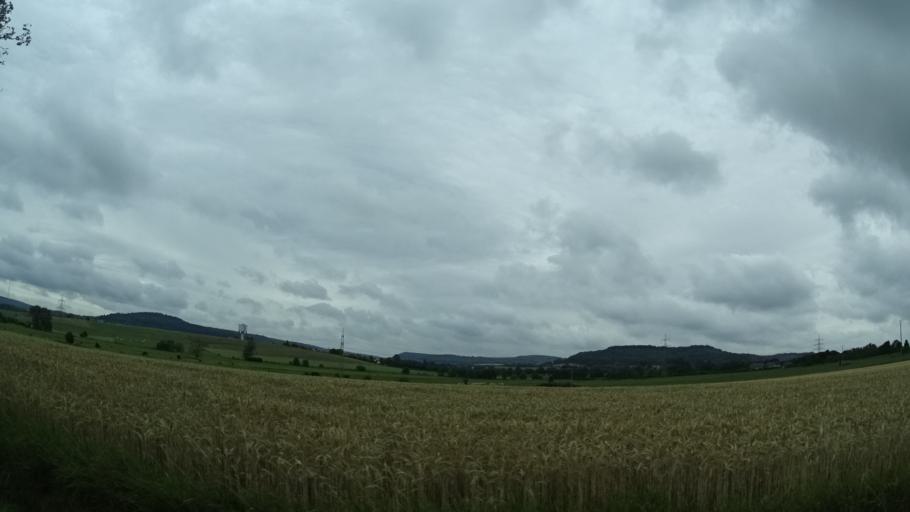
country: LU
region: Luxembourg
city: Bergem
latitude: 49.5193
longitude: 6.0538
